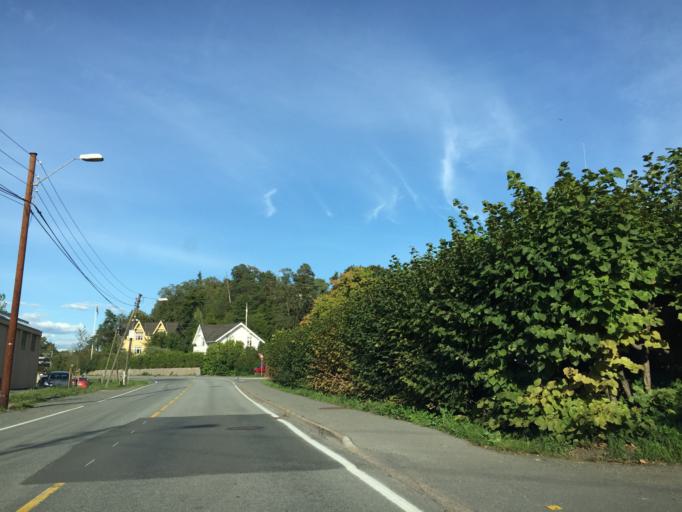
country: NO
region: Akershus
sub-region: Baerum
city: Lysaker
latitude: 59.9062
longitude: 10.6031
